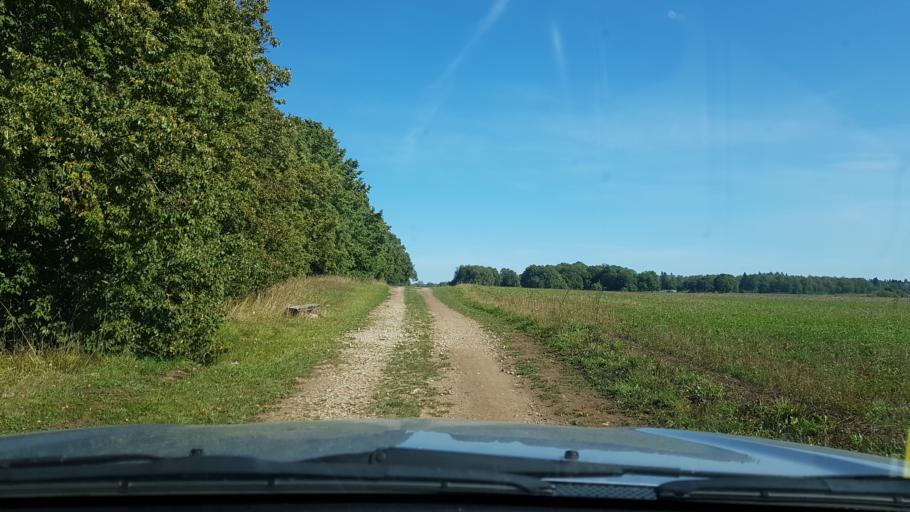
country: EE
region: Ida-Virumaa
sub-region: Sillamaee linn
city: Sillamae
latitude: 59.3945
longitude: 27.8368
